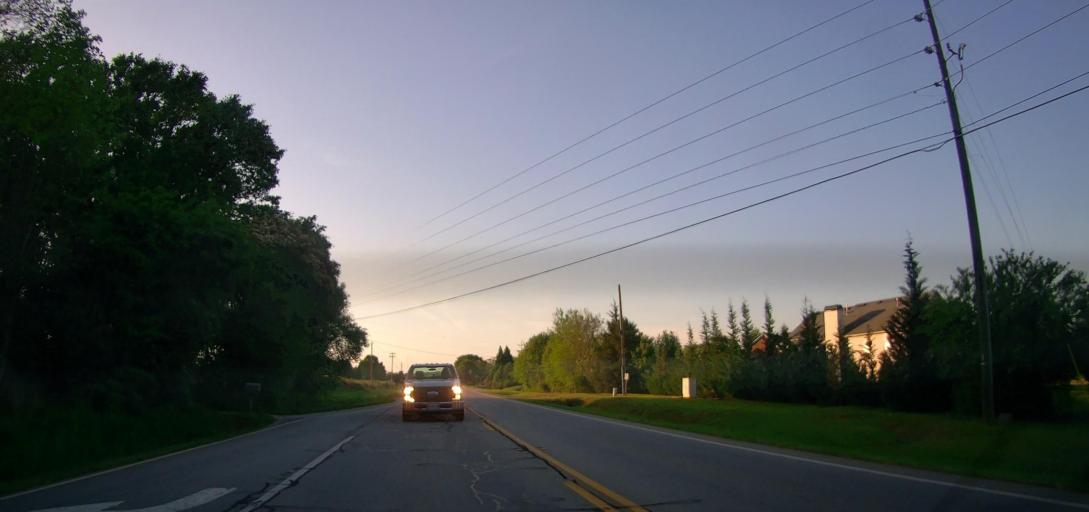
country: US
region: Georgia
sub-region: Newton County
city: Oakwood
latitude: 33.5219
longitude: -83.9504
